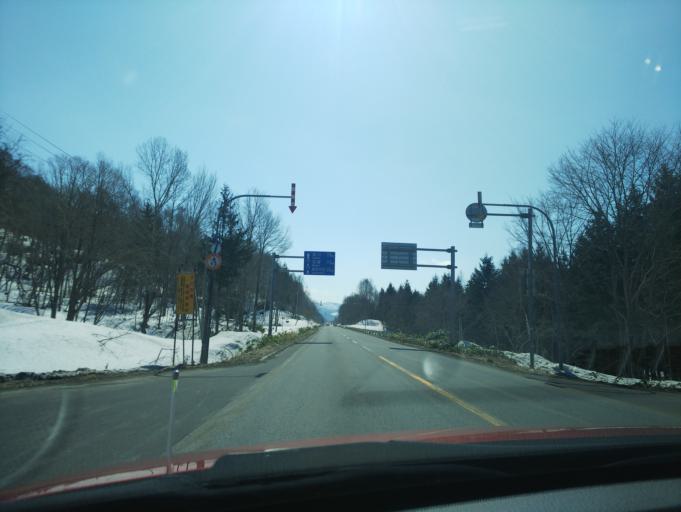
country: JP
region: Hokkaido
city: Nayoro
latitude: 44.6391
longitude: 142.2729
